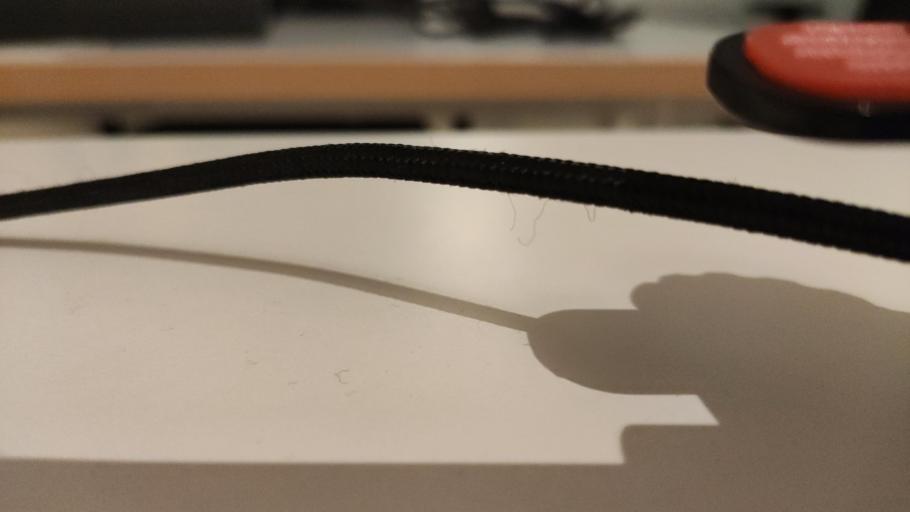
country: RU
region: Moskovskaya
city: Kurovskoye
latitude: 55.5707
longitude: 38.8843
